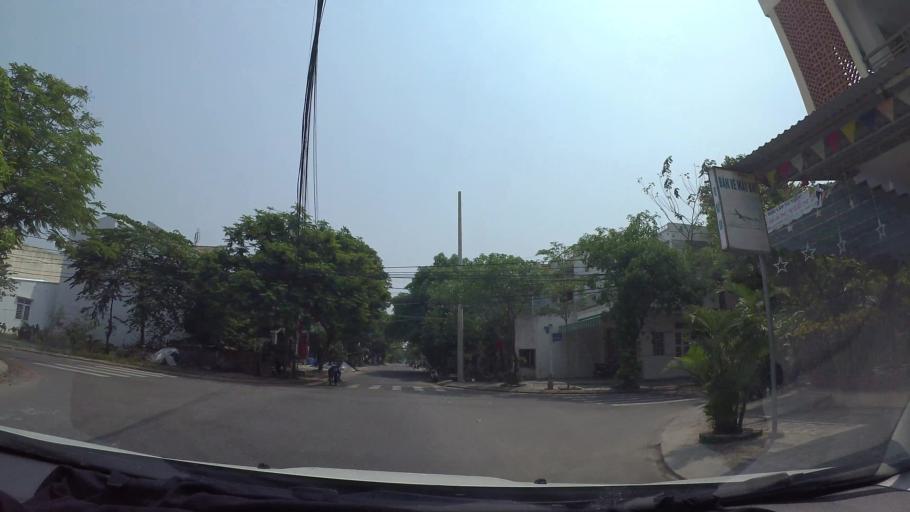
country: VN
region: Da Nang
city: Cam Le
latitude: 15.9995
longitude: 108.2059
